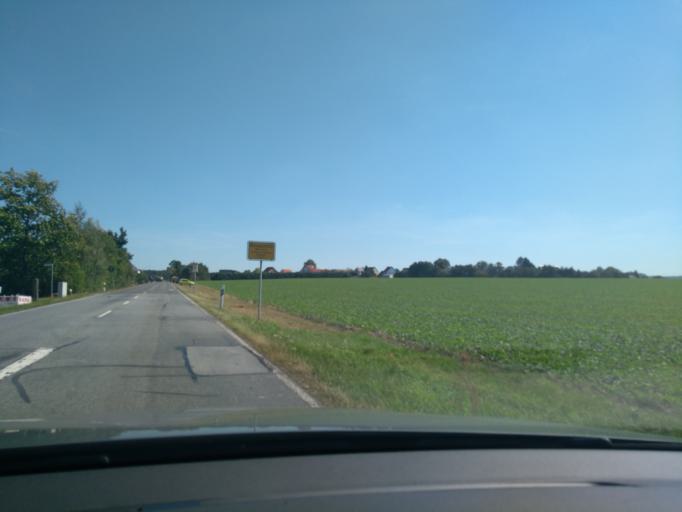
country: DE
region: Saxony
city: Goda
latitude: 51.1916
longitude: 14.3479
